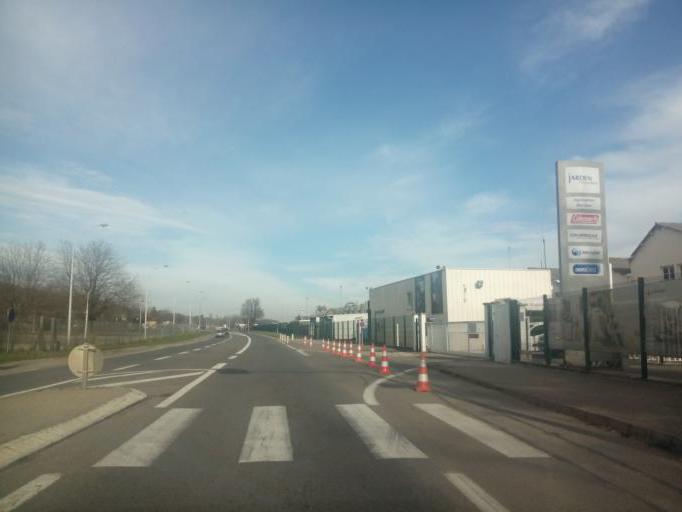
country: FR
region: Rhone-Alpes
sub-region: Departement du Rhone
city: Chaponost
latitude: 45.7016
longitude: 4.7675
